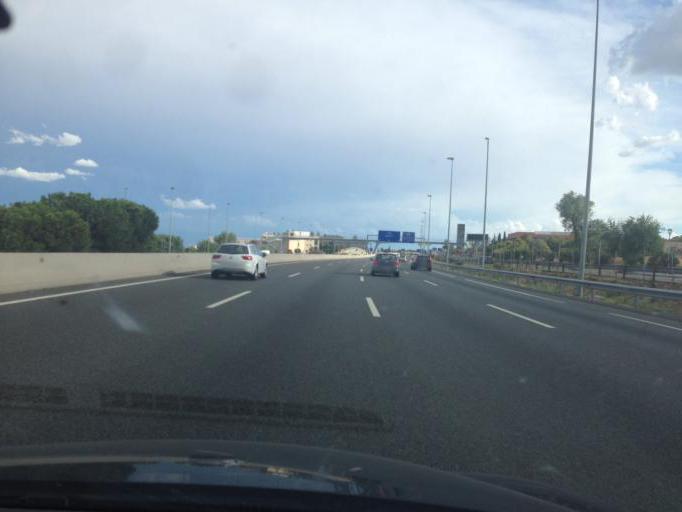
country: ES
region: Madrid
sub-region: Provincia de Madrid
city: Las Matas
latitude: 40.5299
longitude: -3.8873
